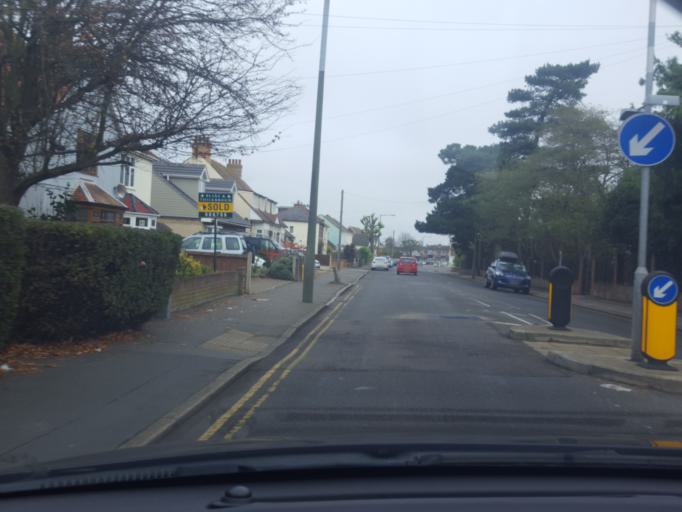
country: GB
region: England
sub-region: Essex
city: Clacton-on-Sea
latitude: 51.7978
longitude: 1.1697
